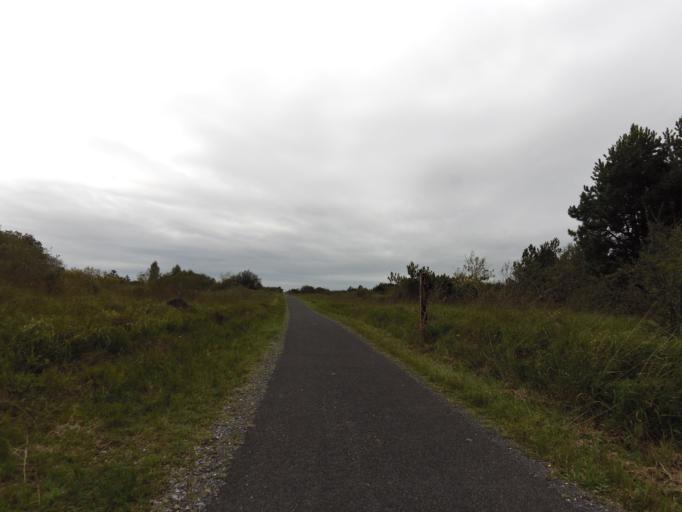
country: IE
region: Leinster
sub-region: Uibh Fhaili
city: Ferbane
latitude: 53.2142
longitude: -7.7573
